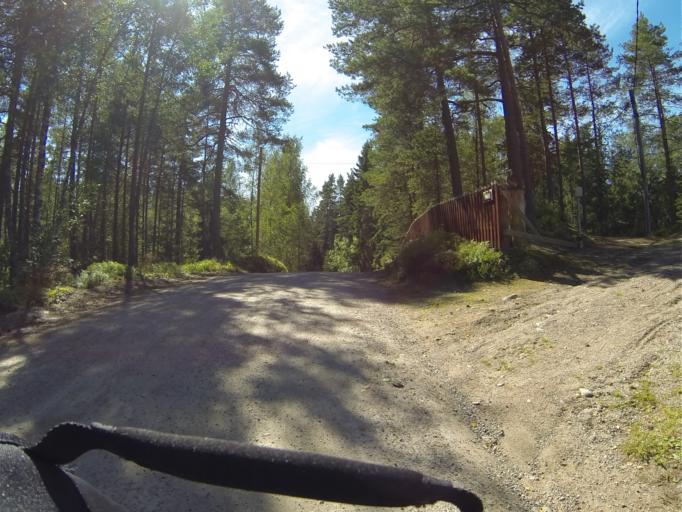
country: FI
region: Varsinais-Suomi
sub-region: Salo
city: Salo
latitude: 60.2943
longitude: 23.0849
